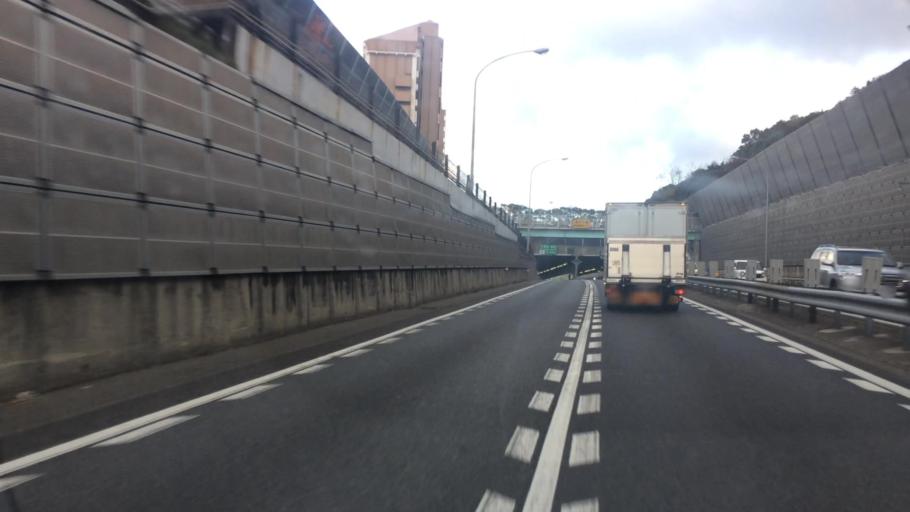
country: JP
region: Hyogo
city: Akashi
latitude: 34.6560
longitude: 135.0344
